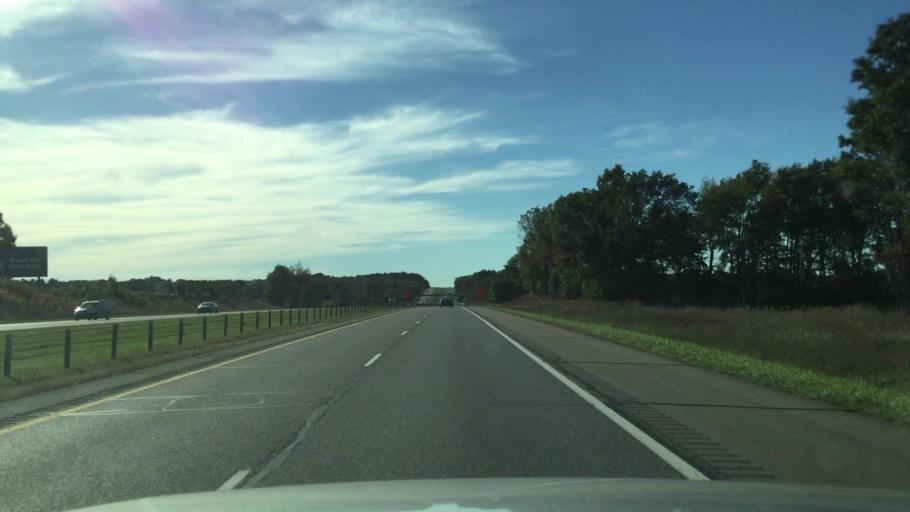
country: US
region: Michigan
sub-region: Calhoun County
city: Albion
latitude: 42.2838
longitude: -84.8132
